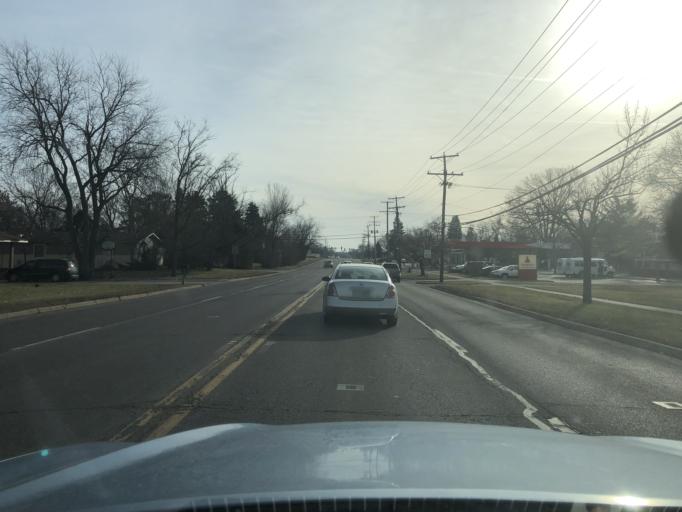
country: US
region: Illinois
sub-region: DuPage County
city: Glendale Heights
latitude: 41.9133
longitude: -88.0815
